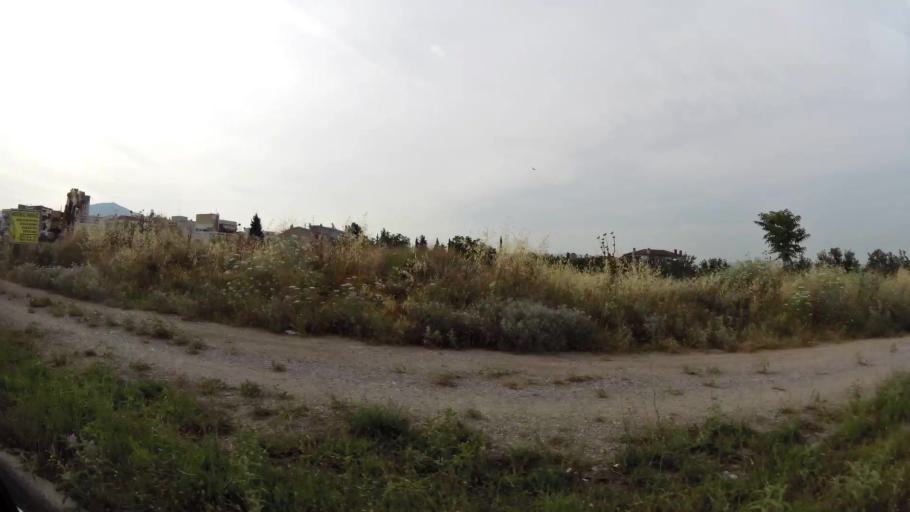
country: GR
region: Central Macedonia
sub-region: Nomos Thessalonikis
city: Thermi
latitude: 40.5521
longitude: 23.0159
